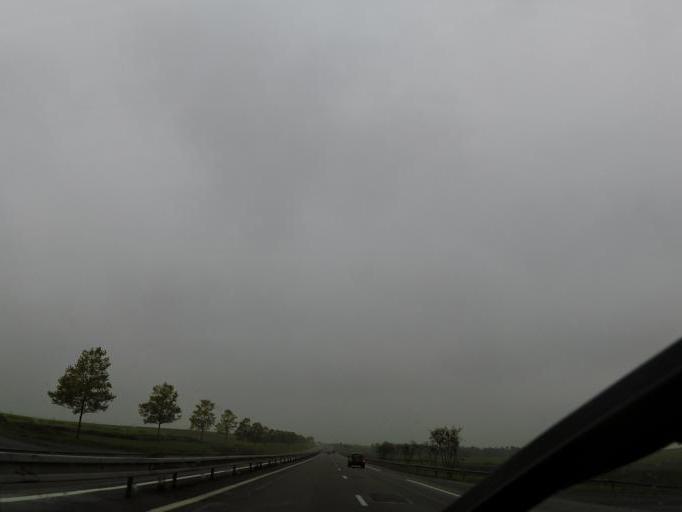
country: FR
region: Champagne-Ardenne
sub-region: Departement de la Marne
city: Suippes
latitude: 49.0601
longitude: 4.7047
